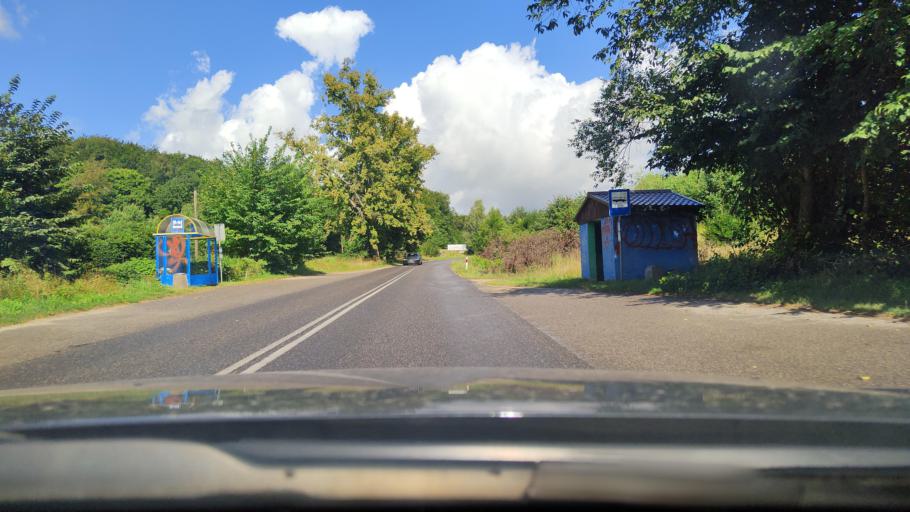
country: PL
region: Pomeranian Voivodeship
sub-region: Powiat pucki
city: Krokowa
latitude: 54.7350
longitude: 18.1607
